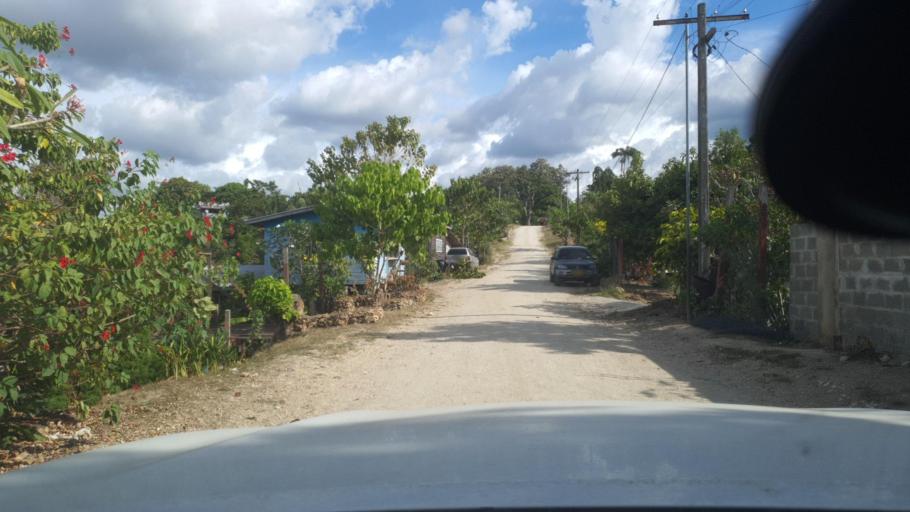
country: SB
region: Guadalcanal
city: Honiara
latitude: -9.4368
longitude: 159.9495
